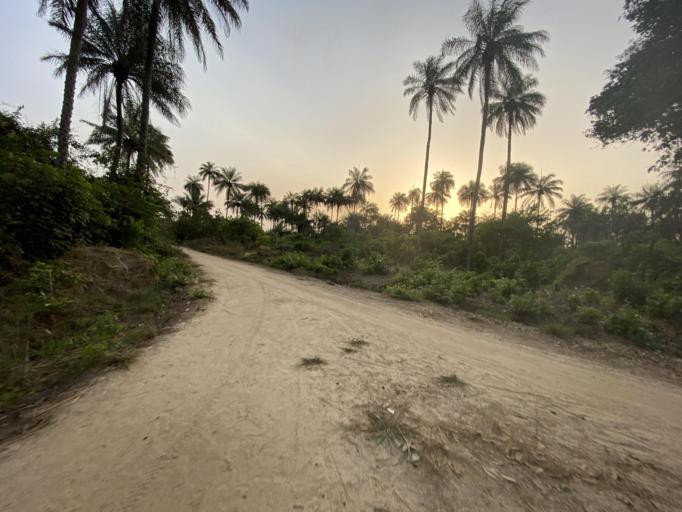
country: GW
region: Tombali
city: Quebo
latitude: 10.8956
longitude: -15.0140
